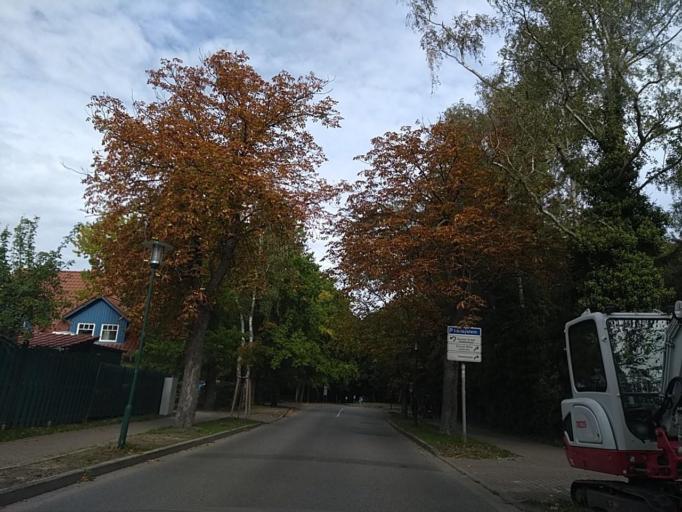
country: DE
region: Mecklenburg-Vorpommern
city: Seeheilbad Graal-Muritz
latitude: 54.2518
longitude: 12.2434
